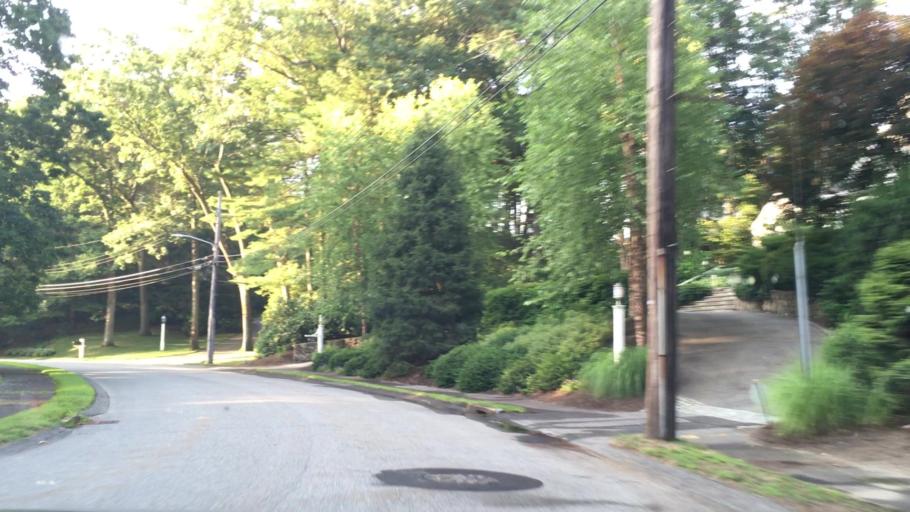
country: US
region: Massachusetts
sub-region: Norfolk County
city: Wellesley
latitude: 42.3209
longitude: -71.2952
